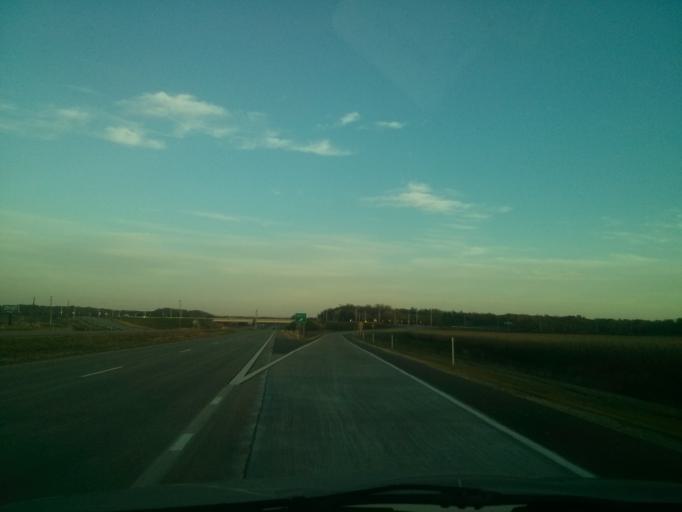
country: US
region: Wisconsin
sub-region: Pierce County
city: River Falls
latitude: 44.9010
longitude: -92.6537
